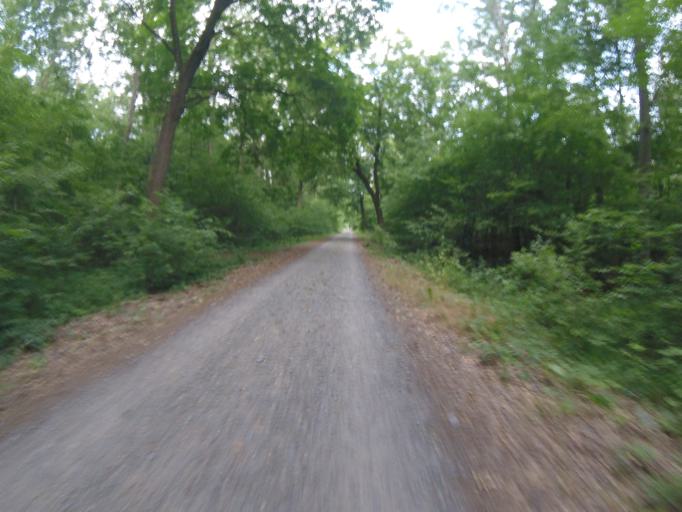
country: DE
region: Brandenburg
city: Konigs Wusterhausen
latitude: 52.3062
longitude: 13.6093
